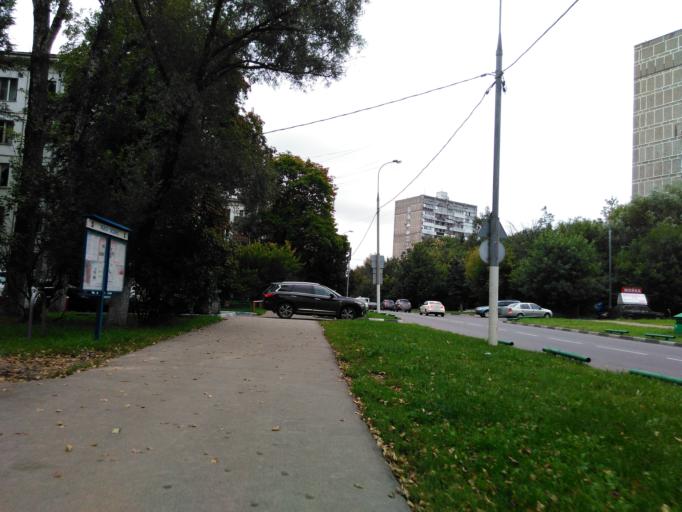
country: RU
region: Moscow
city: Zyuzino
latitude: 55.6627
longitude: 37.5825
